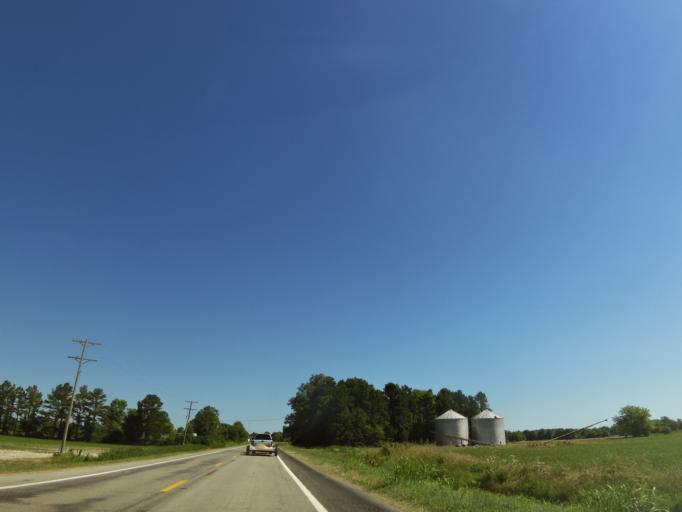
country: US
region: Arkansas
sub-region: Clay County
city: Piggott
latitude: 36.4420
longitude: -90.1472
